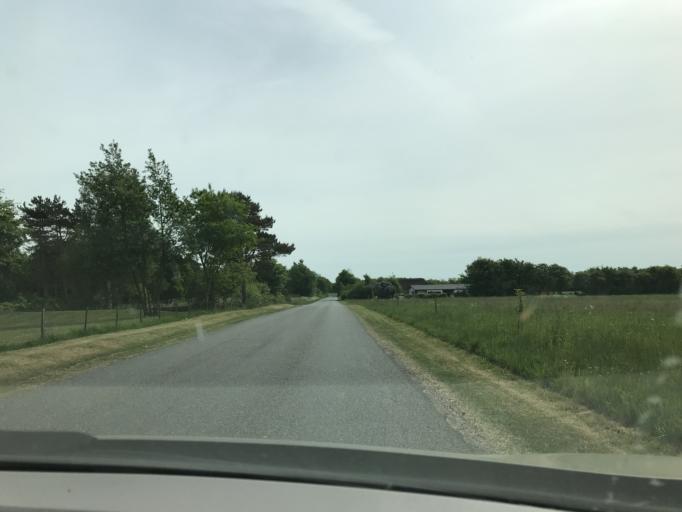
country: DK
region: Central Jutland
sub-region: Norddjurs Kommune
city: Allingabro
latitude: 56.5950
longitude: 10.3121
